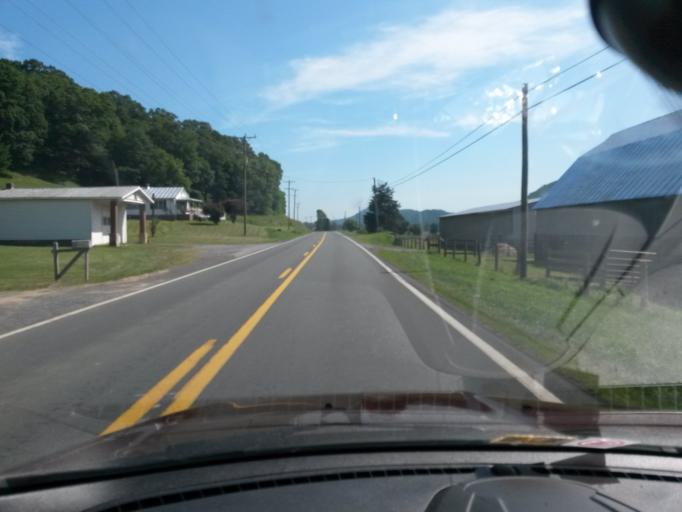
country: US
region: West Virginia
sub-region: Hardy County
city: Moorefield
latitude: 39.0244
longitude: -78.7586
